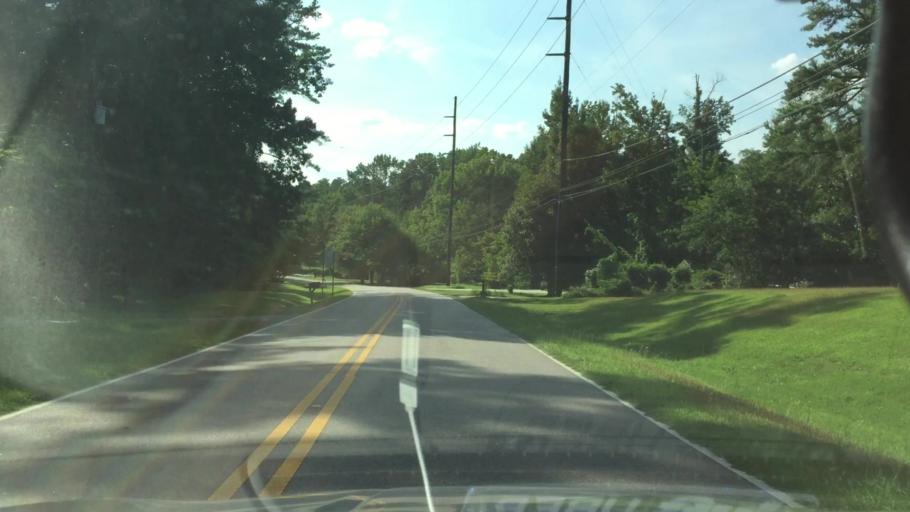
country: US
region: Alabama
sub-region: Lee County
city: Auburn
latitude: 32.5927
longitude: -85.4664
